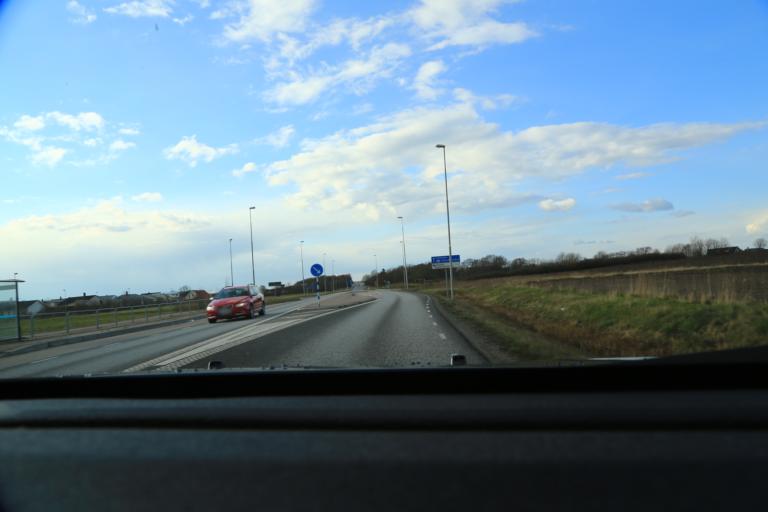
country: SE
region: Halland
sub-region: Varbergs Kommun
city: Traslovslage
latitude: 57.0629
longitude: 12.2947
